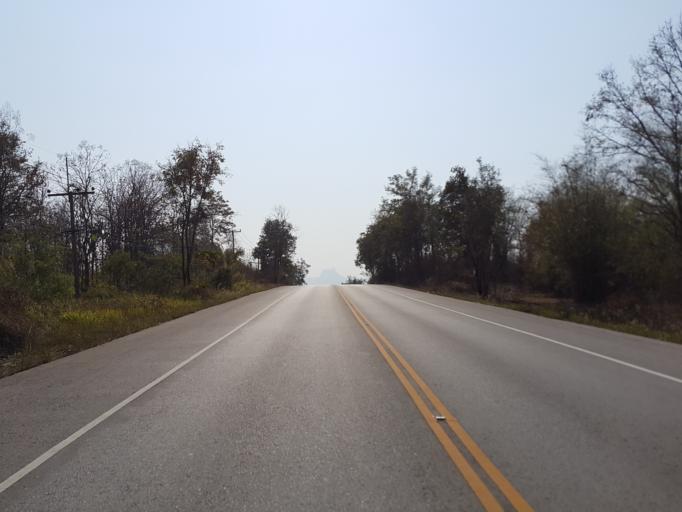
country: TH
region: Lampang
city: Mueang Pan
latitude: 18.8355
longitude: 99.6018
